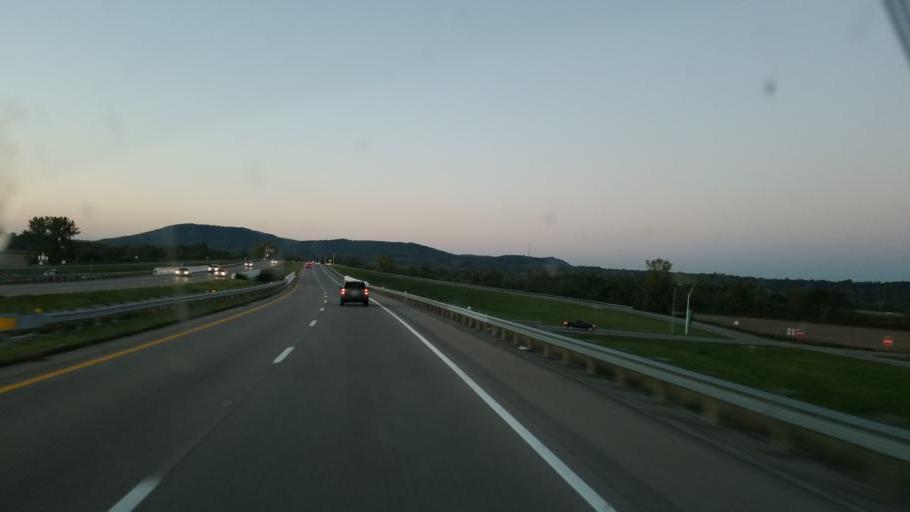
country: US
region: Ohio
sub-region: Ross County
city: Chillicothe
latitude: 39.3132
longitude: -82.9393
